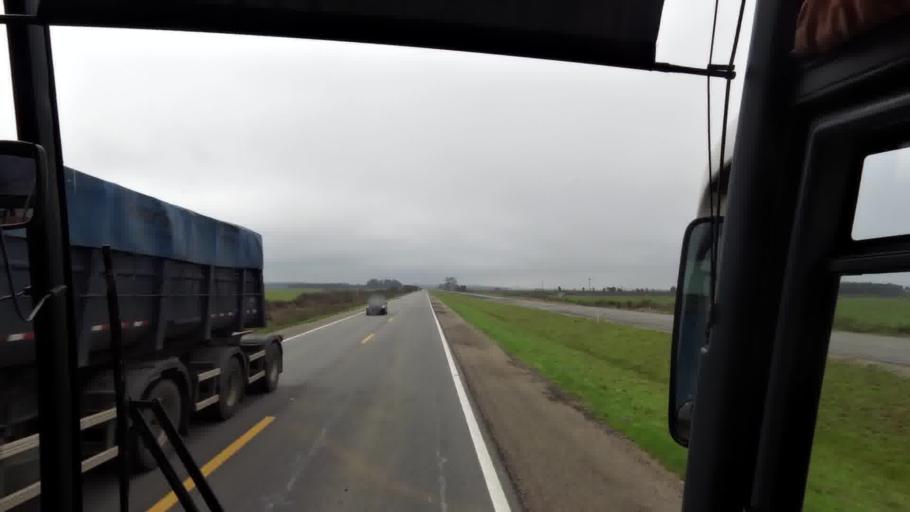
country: BR
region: Rio Grande do Sul
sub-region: Pelotas
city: Pelotas
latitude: -31.5953
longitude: -52.2869
